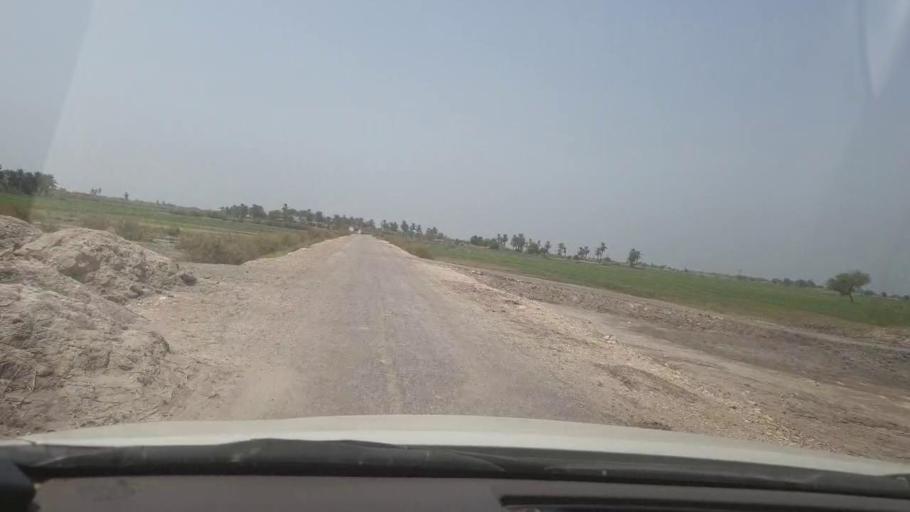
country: PK
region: Sindh
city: Garhi Yasin
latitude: 27.9773
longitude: 68.5467
